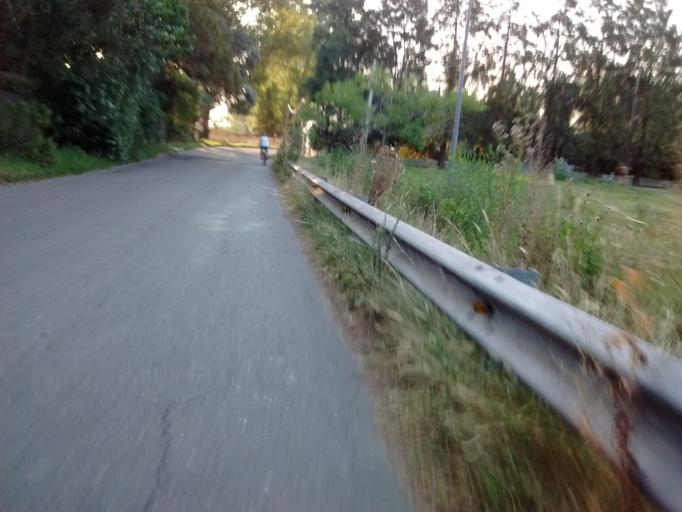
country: AR
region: Santa Fe
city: Funes
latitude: -32.9198
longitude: -60.7586
